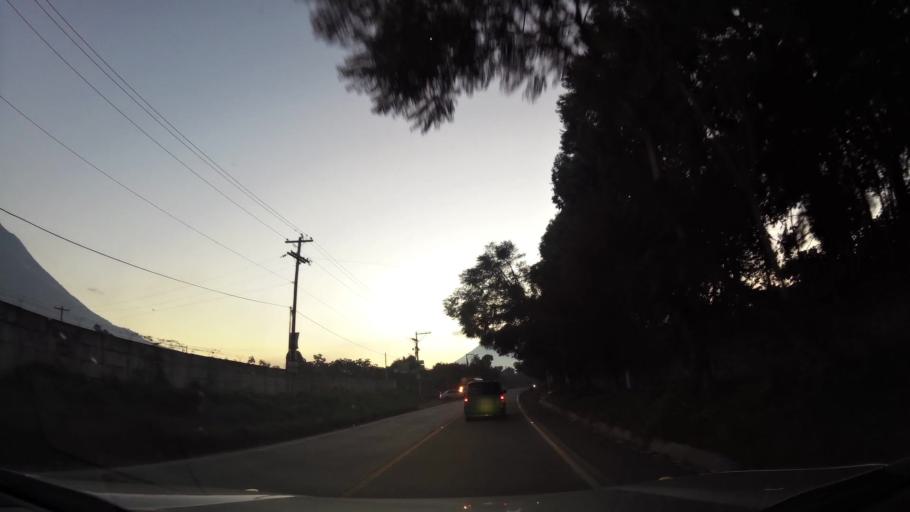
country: GT
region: Sacatepequez
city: Ciudad Vieja
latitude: 14.5314
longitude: -90.7516
